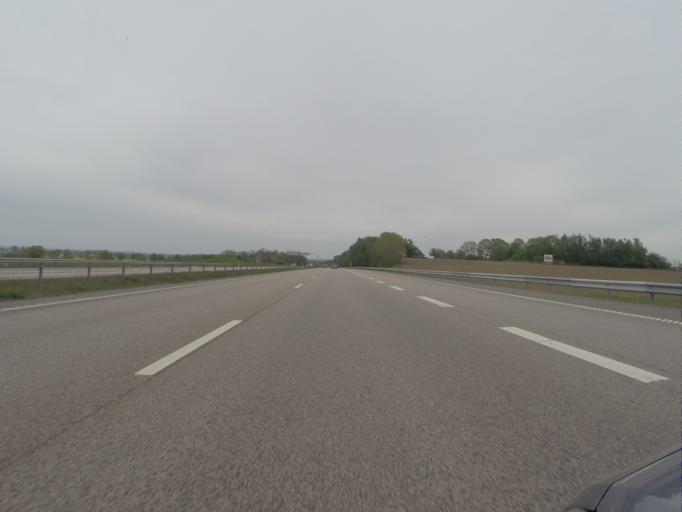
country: SE
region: Skane
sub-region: Helsingborg
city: Odakra
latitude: 56.0875
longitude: 12.7894
